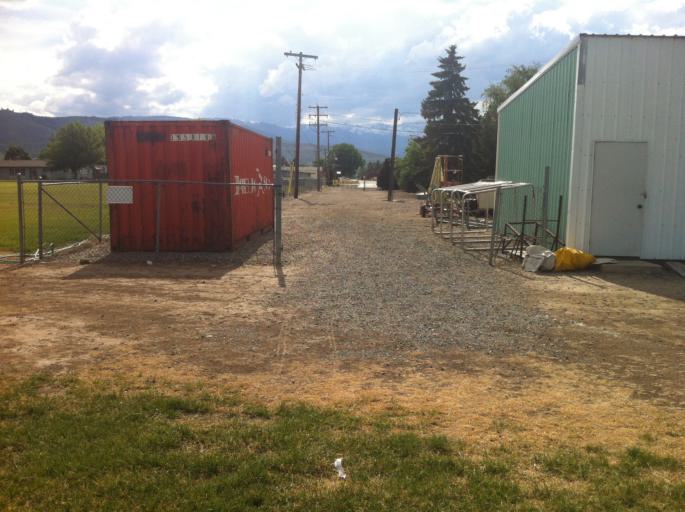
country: US
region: Oregon
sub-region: Baker County
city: Baker City
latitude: 44.7890
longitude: -117.8371
